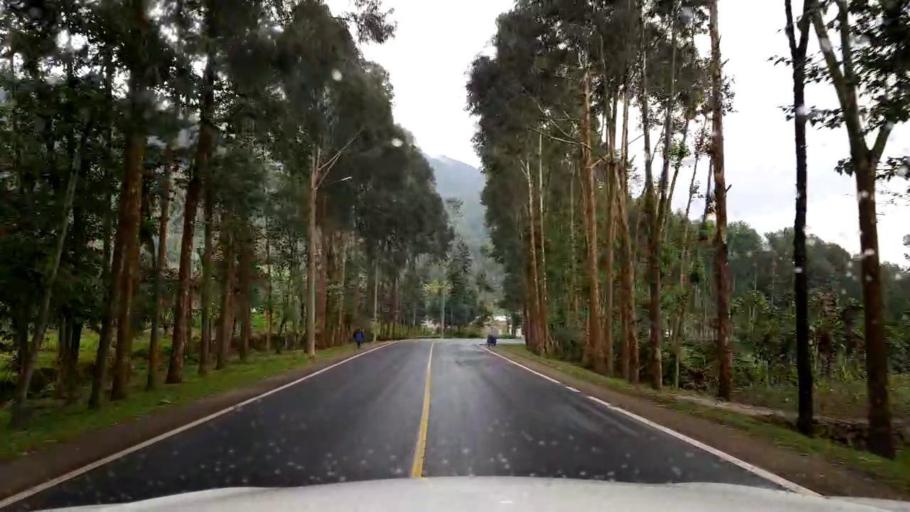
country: RW
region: Western Province
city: Gisenyi
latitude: -1.6700
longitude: 29.3620
